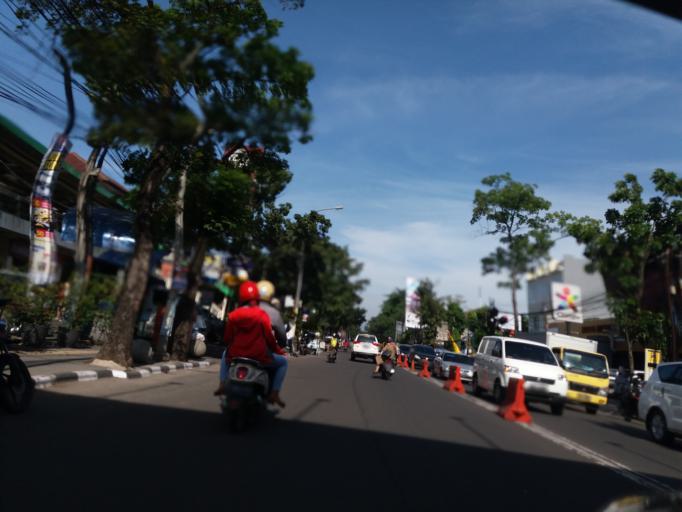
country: ID
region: West Java
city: Bandung
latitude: -6.9410
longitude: 107.6267
